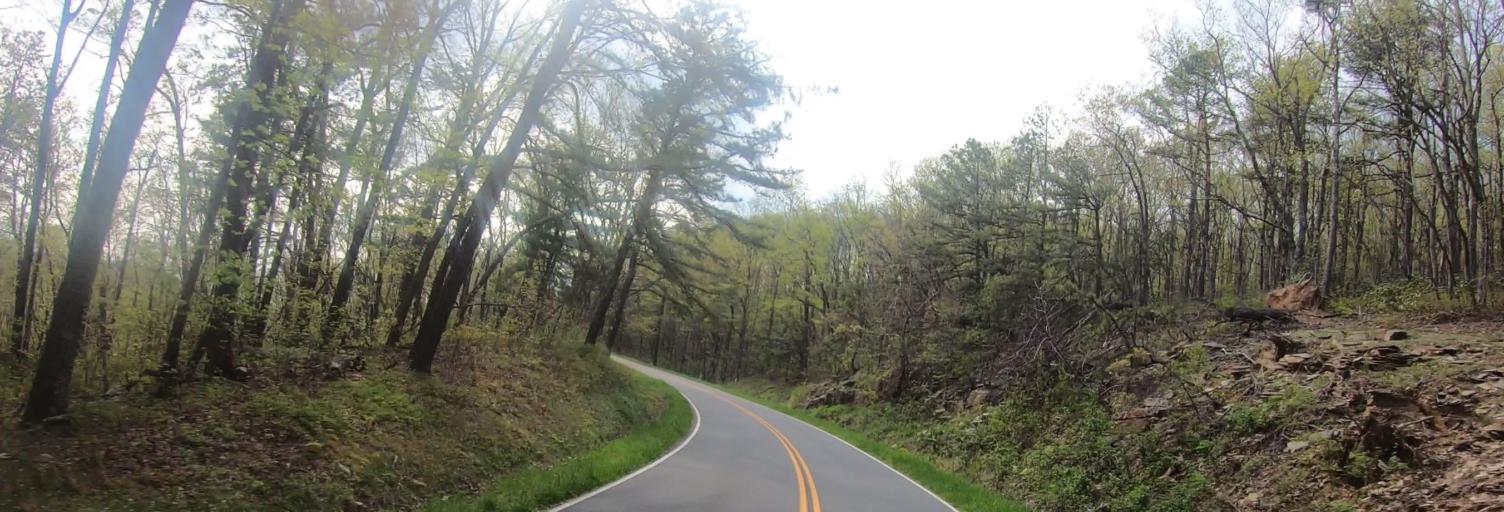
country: US
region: Virginia
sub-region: Augusta County
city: Dooms
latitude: 38.1059
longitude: -78.7804
